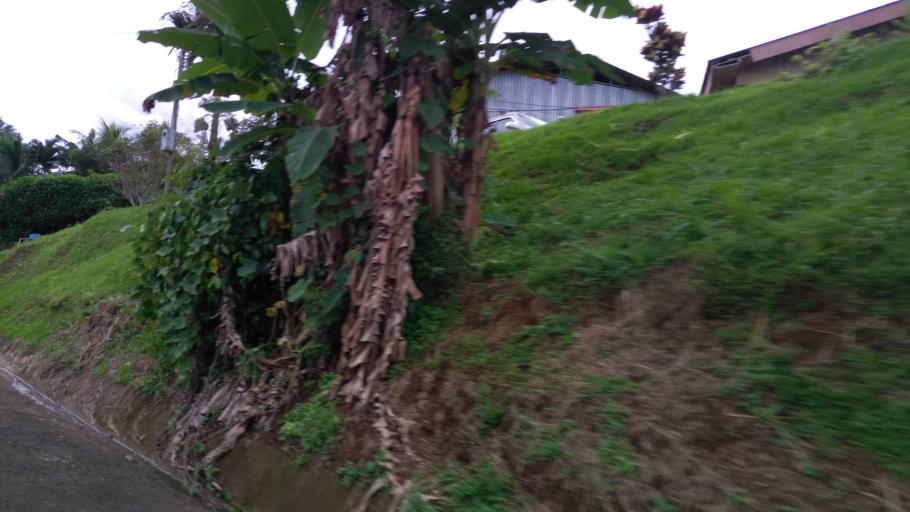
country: CR
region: Alajuela
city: Pocosol
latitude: 10.3646
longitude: -84.5869
